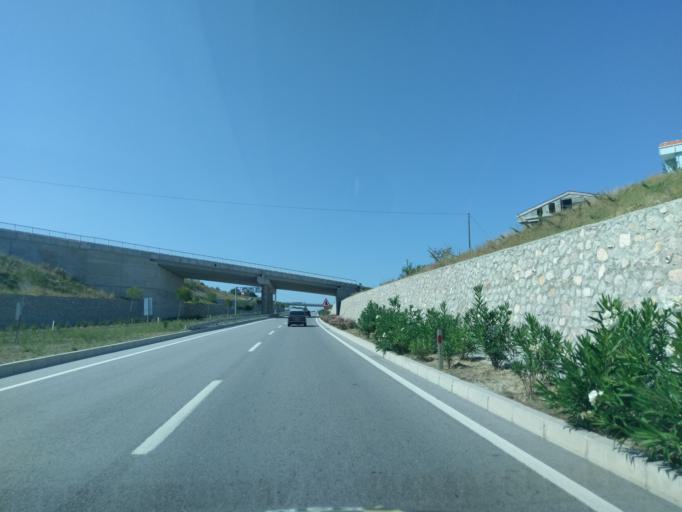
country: TR
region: Sinop
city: Gerze
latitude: 41.7914
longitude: 35.1891
